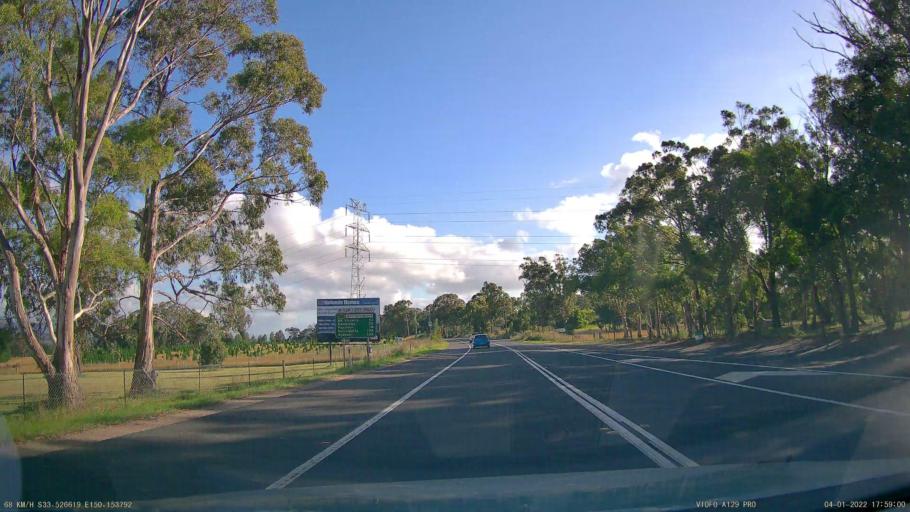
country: AU
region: New South Wales
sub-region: Lithgow
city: Bowenfels
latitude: -33.5269
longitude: 150.1537
